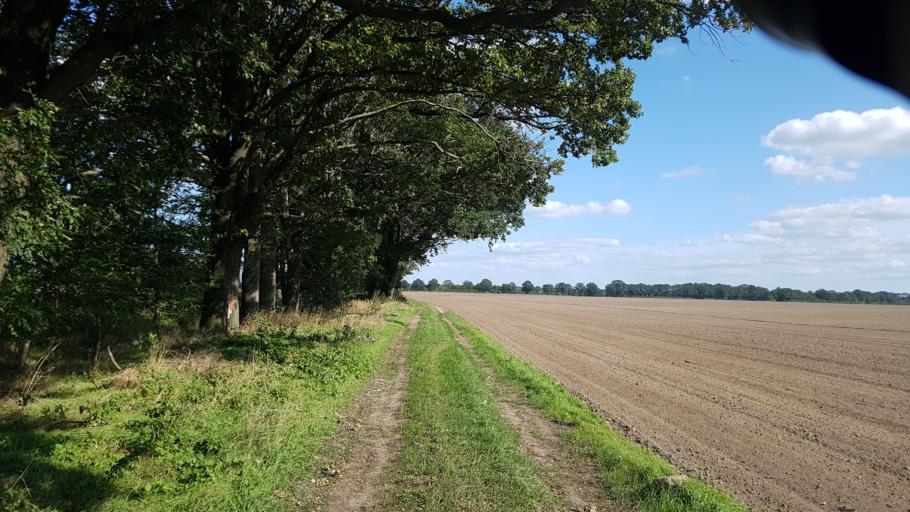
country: DE
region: Brandenburg
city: Sonnewalde
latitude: 51.6883
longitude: 13.6526
